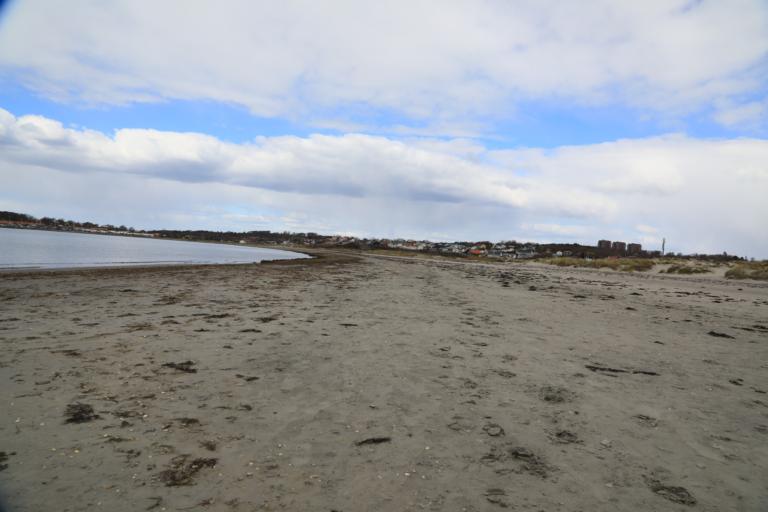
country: SE
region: Halland
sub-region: Varbergs Kommun
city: Traslovslage
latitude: 57.0797
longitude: 12.2605
